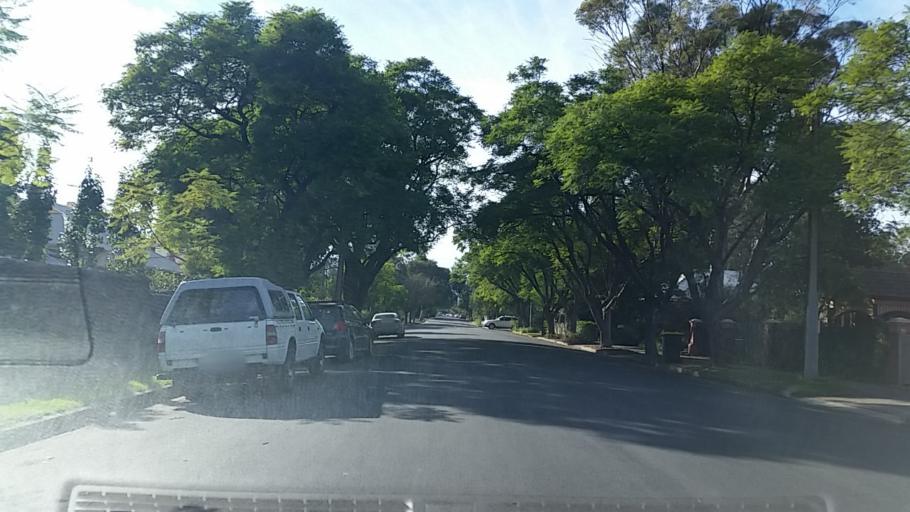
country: AU
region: South Australia
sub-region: Mitcham
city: Hawthorn
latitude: -34.9697
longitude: 138.6018
